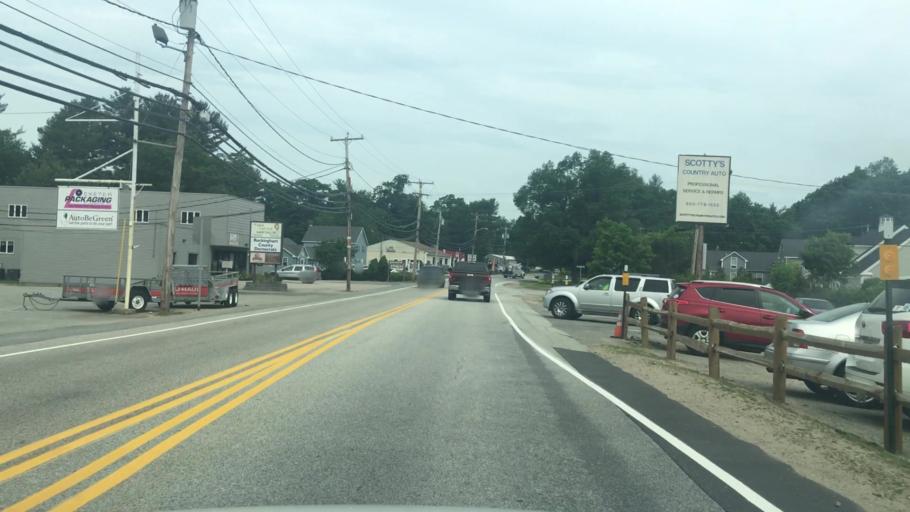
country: US
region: New Hampshire
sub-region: Rockingham County
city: Exeter
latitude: 42.9888
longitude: -70.9667
